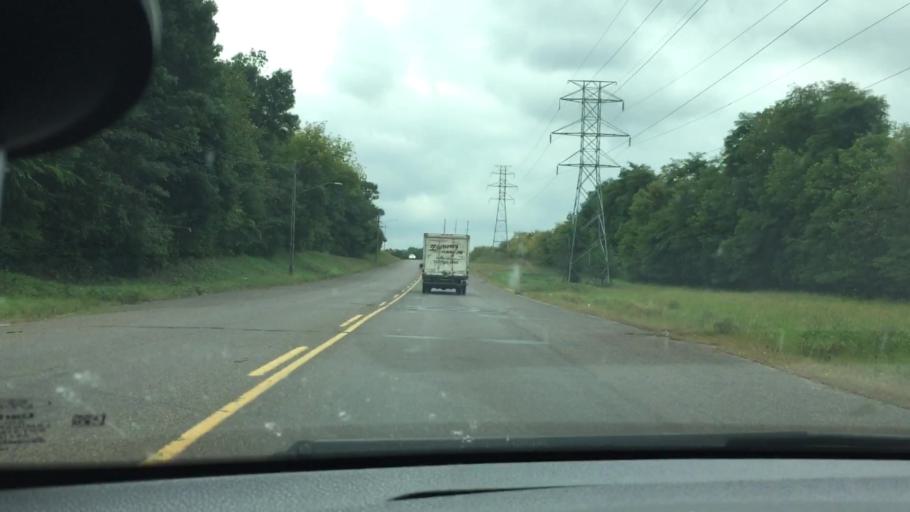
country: US
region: Wisconsin
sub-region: Chippewa County
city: Chippewa Falls
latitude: 44.9222
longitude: -91.3934
